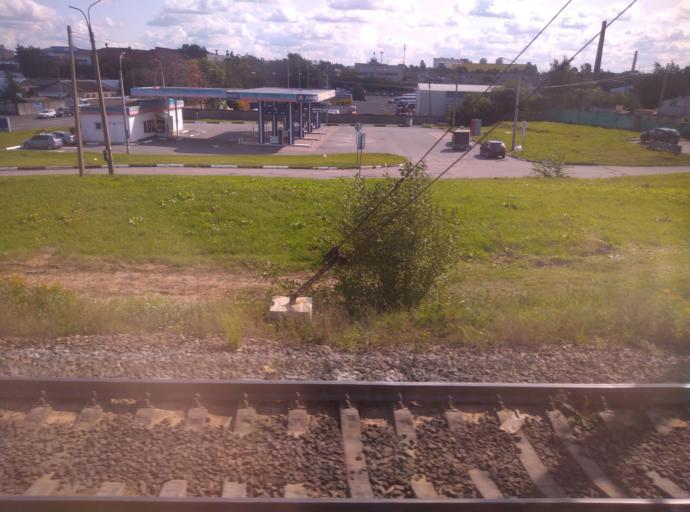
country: RU
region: St.-Petersburg
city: Centralniy
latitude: 59.9050
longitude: 30.3815
